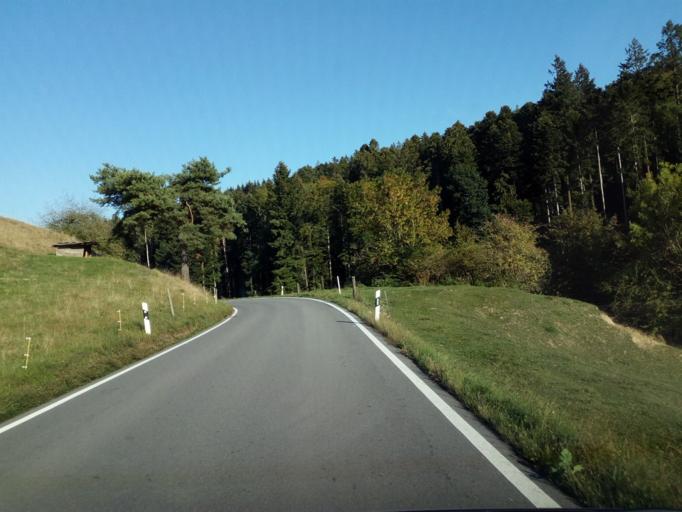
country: CH
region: Bern
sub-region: Seeland District
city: Schupfen
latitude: 47.0304
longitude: 7.3791
